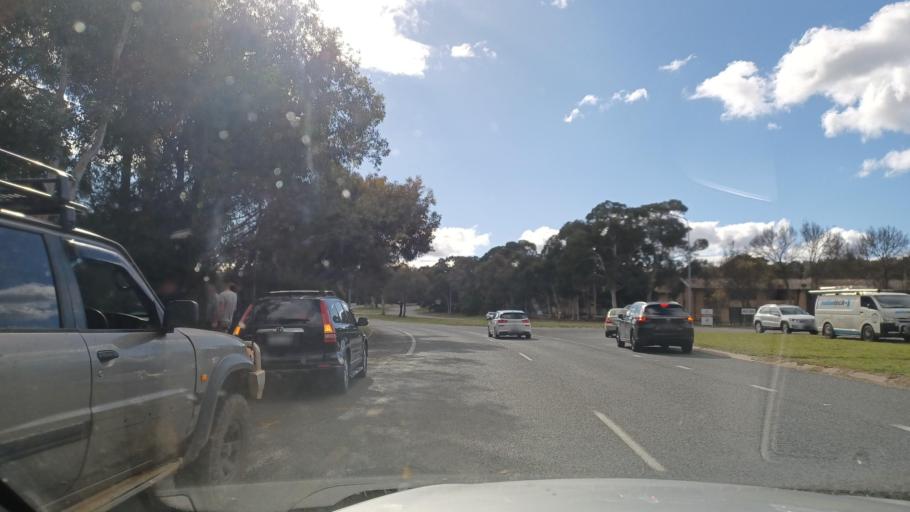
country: AU
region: Australian Capital Territory
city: Belconnen
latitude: -35.2109
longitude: 149.0481
